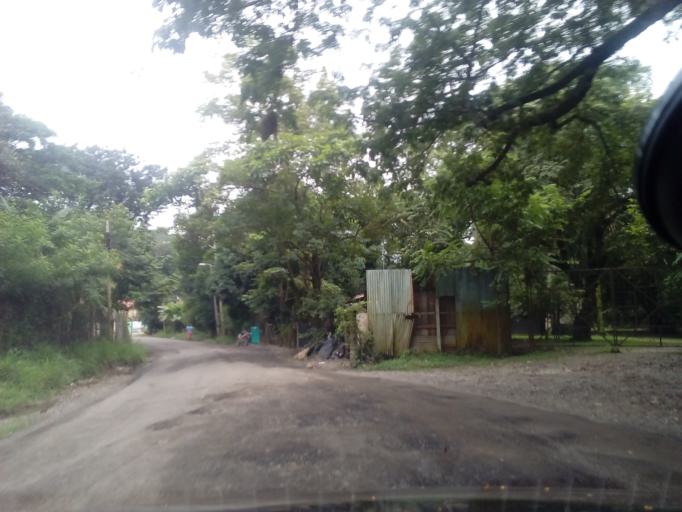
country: CR
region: Guanacaste
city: Samara
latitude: 9.9394
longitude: -85.6551
